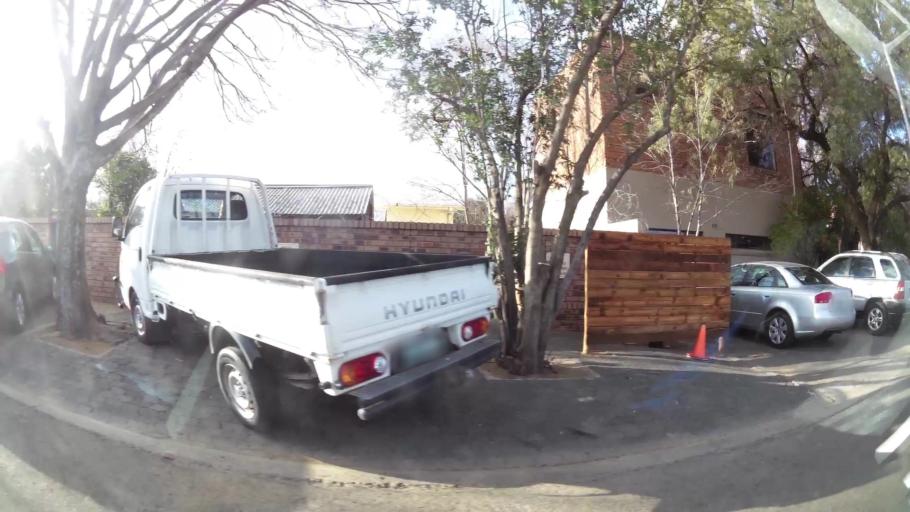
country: ZA
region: Orange Free State
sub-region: Mangaung Metropolitan Municipality
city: Bloemfontein
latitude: -29.1067
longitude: 26.1947
